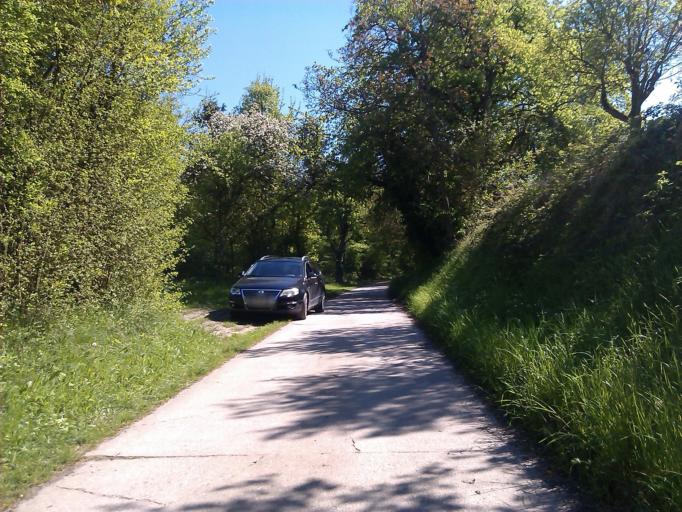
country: DE
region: Baden-Wuerttemberg
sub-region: Karlsruhe Region
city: Sulzfeld
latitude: 49.0918
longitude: 8.8659
